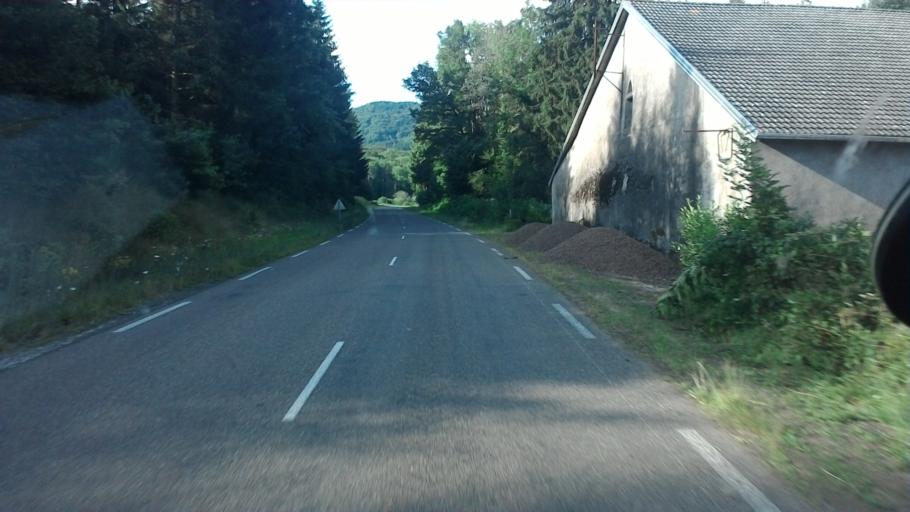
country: FR
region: Lorraine
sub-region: Departement des Vosges
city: Rupt-sur-Moselle
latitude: 47.8707
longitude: 6.5729
